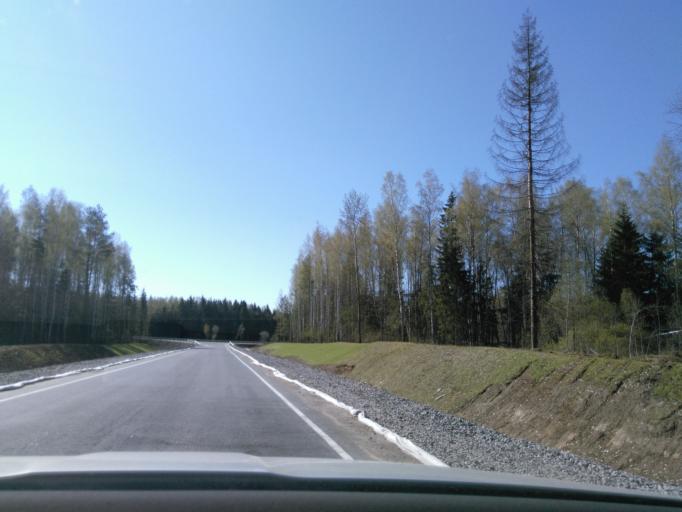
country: RU
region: Moskovskaya
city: Mendeleyevo
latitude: 56.0632
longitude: 37.2319
